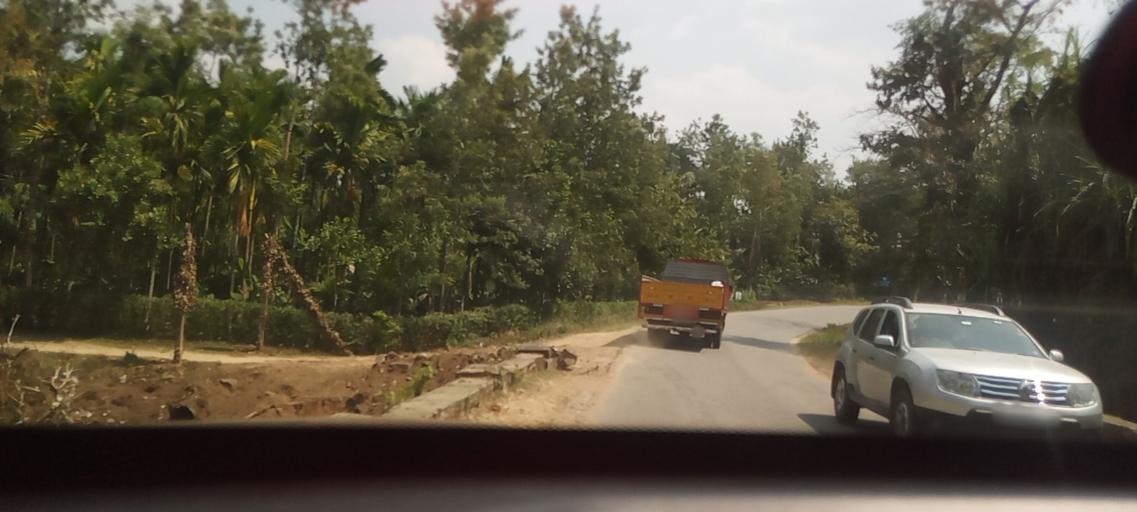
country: IN
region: Karnataka
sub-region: Chikmagalur
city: Mudigere
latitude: 13.3198
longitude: 75.5675
